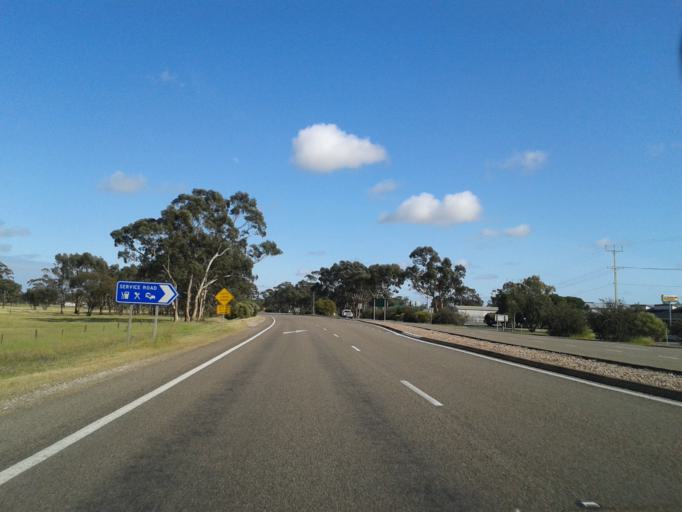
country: AU
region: South Australia
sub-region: Tatiara
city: Bordertown
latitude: -36.3001
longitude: 140.7595
